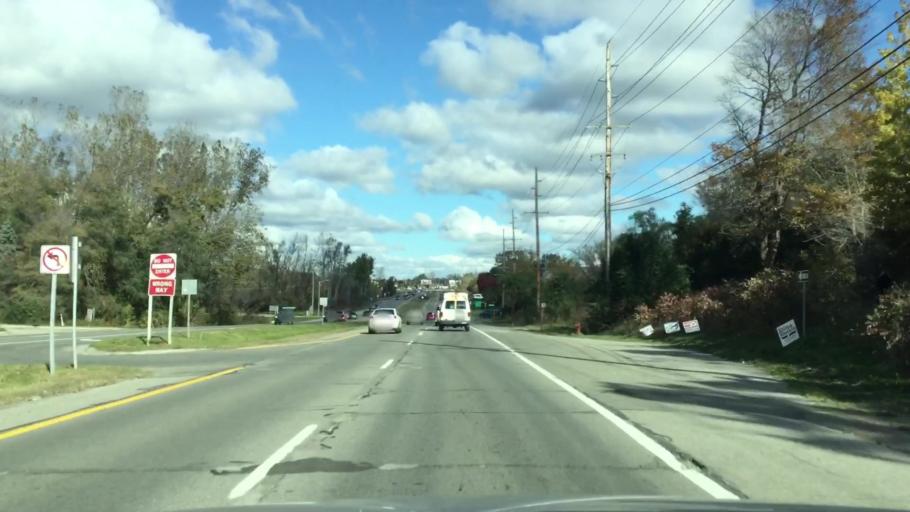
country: US
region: Michigan
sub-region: Oakland County
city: Lake Orion
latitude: 42.7952
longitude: -83.2465
